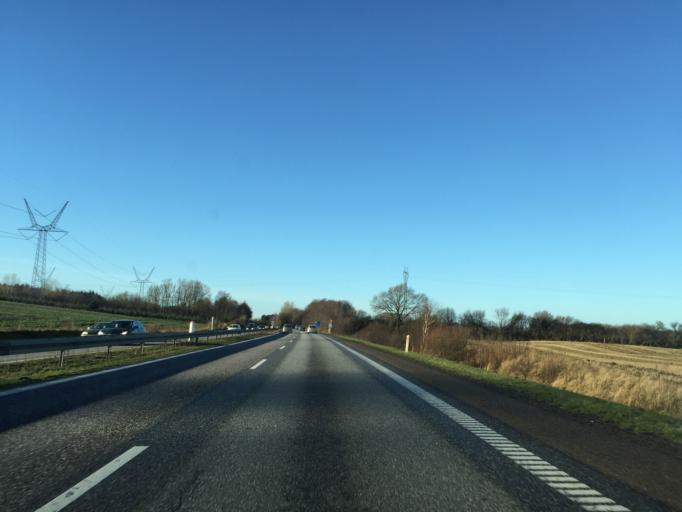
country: DK
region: South Denmark
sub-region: Odense Kommune
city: Bellinge
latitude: 55.3807
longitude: 10.2793
